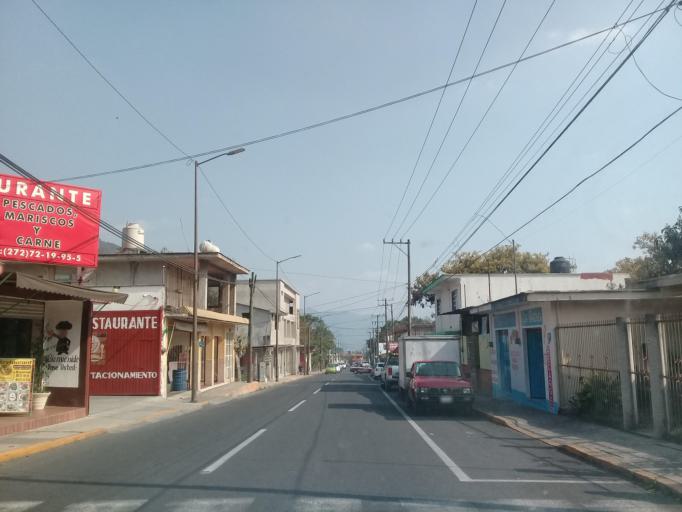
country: MX
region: Veracruz
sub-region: Mariano Escobedo
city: Palmira
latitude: 18.8733
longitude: -97.1041
